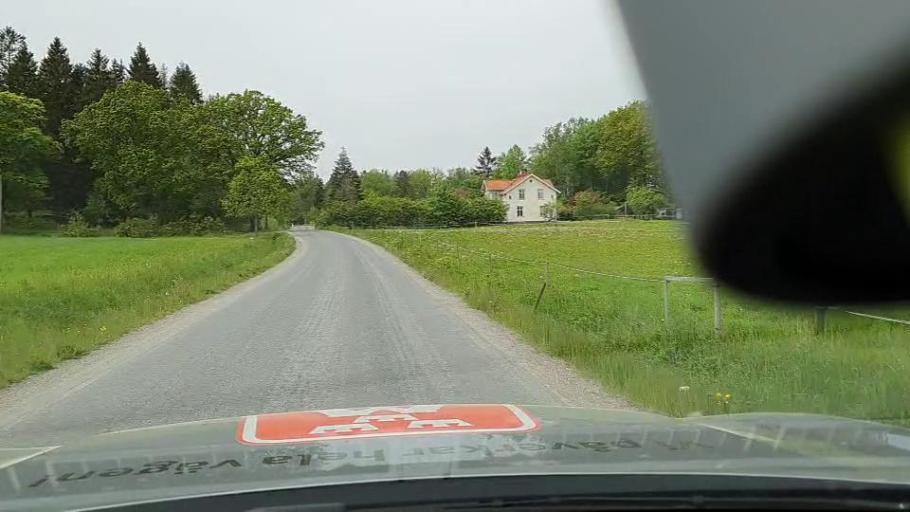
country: SE
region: Soedermanland
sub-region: Flens Kommun
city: Flen
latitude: 59.1032
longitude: 16.5472
